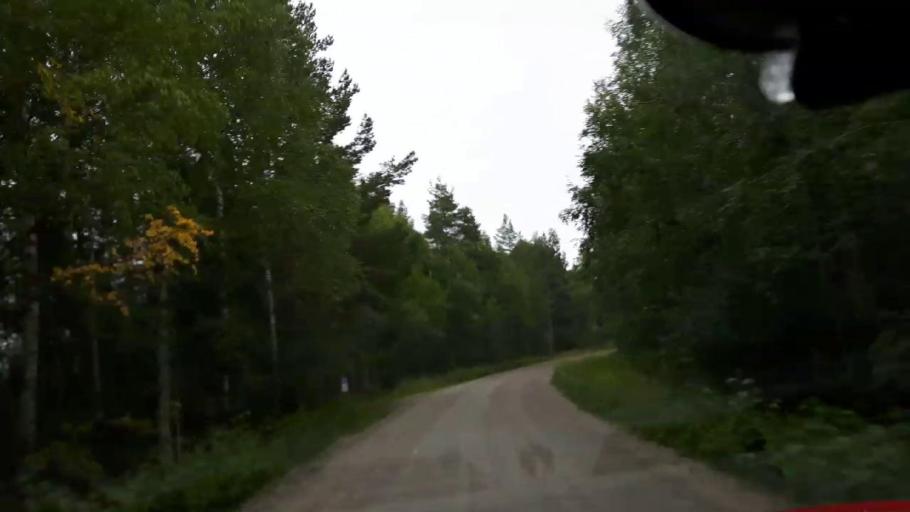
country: SE
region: Vaesternorrland
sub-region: Ange Kommun
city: Ange
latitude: 62.8029
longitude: 15.7669
